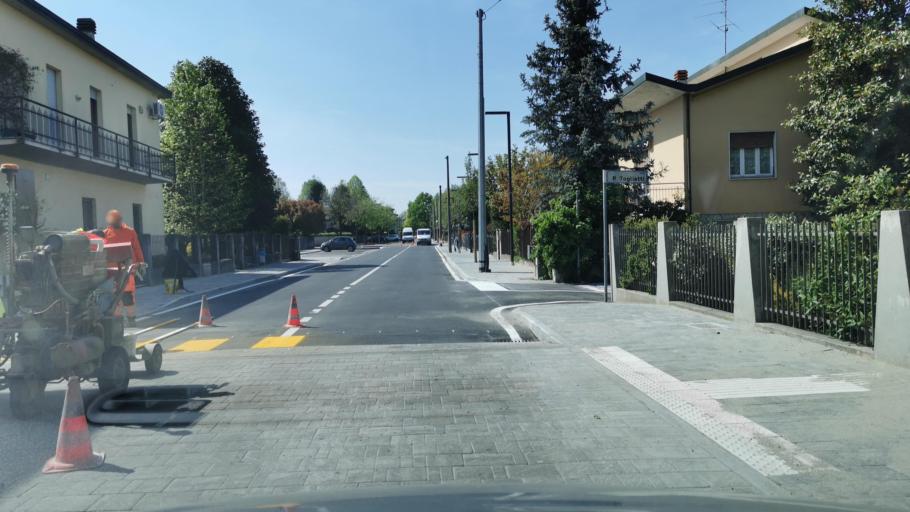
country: IT
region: Emilia-Romagna
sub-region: Provincia di Piacenza
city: Castelvetro Piacentino
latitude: 45.0965
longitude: 9.9861
